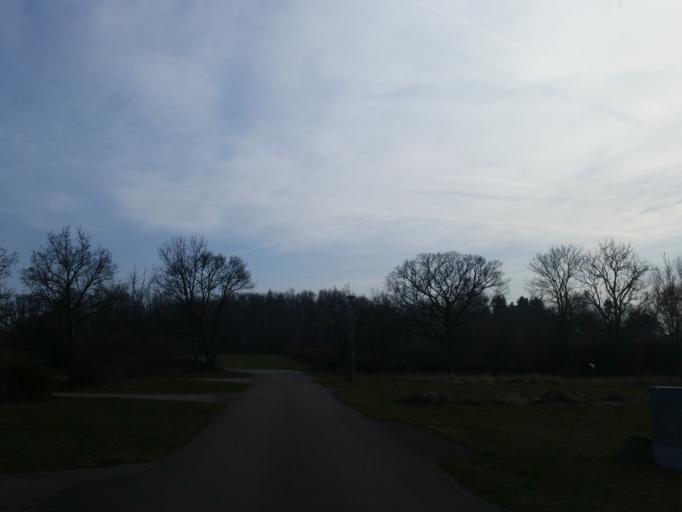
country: SE
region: Kalmar
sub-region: Borgholms Kommun
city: Borgholm
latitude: 56.9063
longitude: 16.7284
